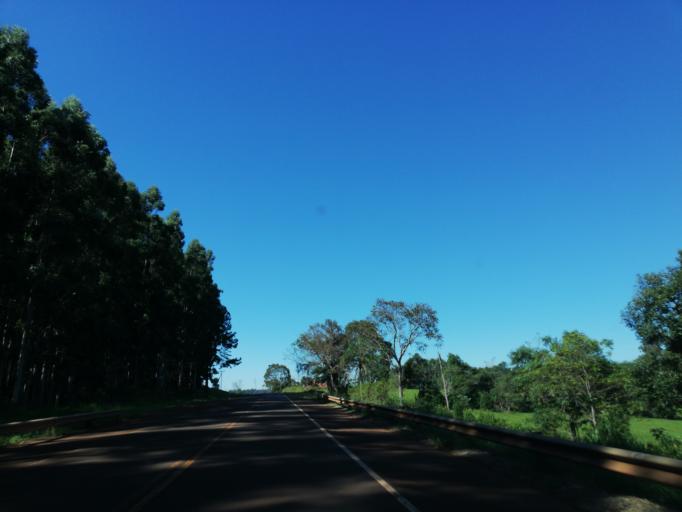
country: AR
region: Misiones
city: Dos de Mayo
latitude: -27.0725
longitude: -54.4074
